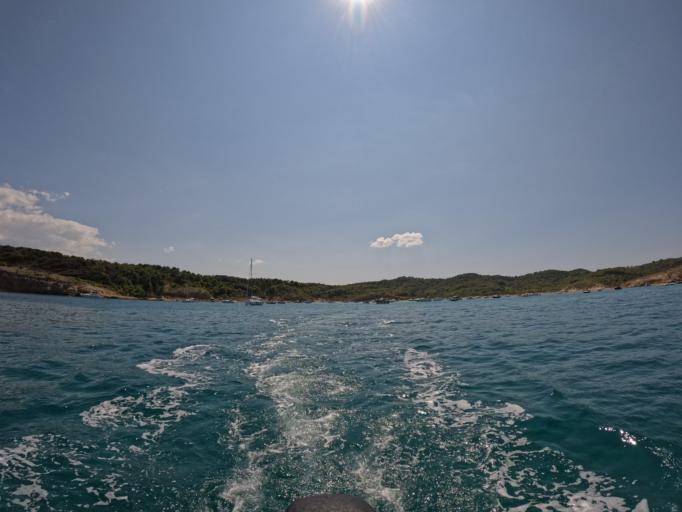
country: HR
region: Primorsko-Goranska
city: Lopar
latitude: 44.8442
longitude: 14.7552
